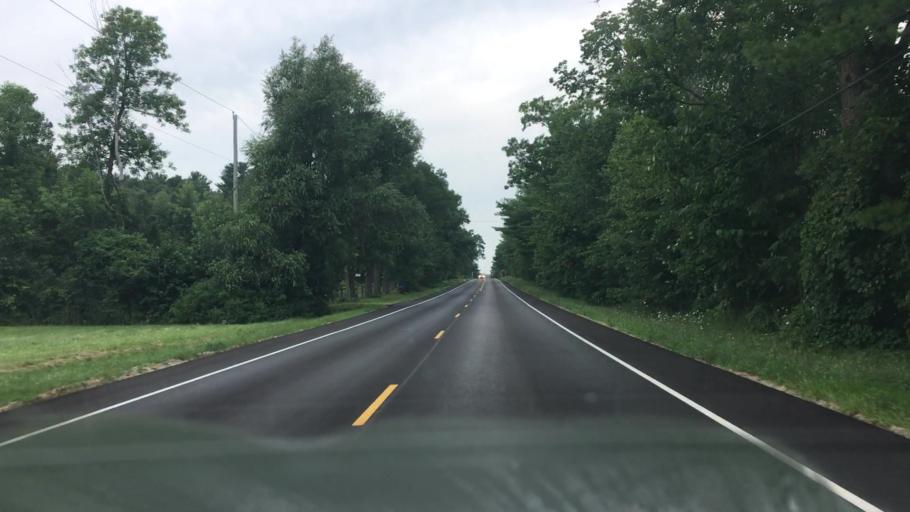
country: US
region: New York
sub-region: Clinton County
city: Morrisonville
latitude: 44.6499
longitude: -73.5497
